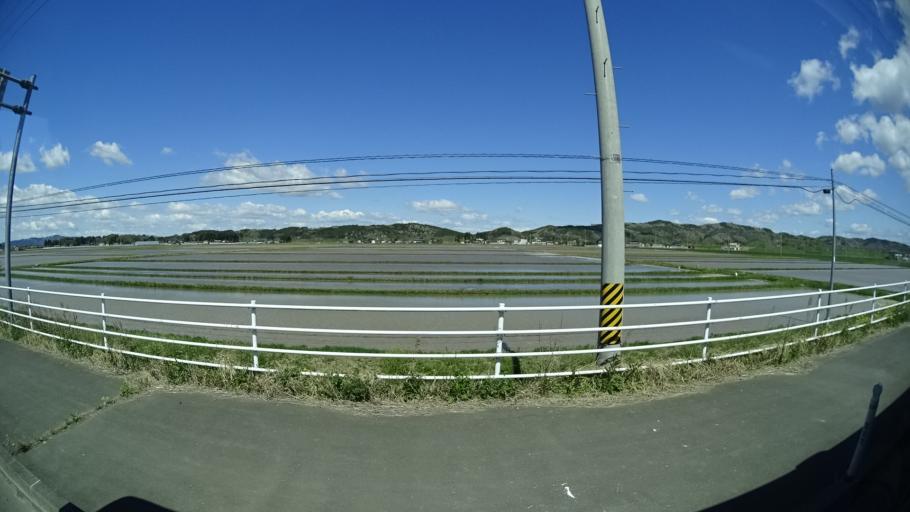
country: JP
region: Miyagi
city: Wakuya
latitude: 38.5986
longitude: 141.2794
